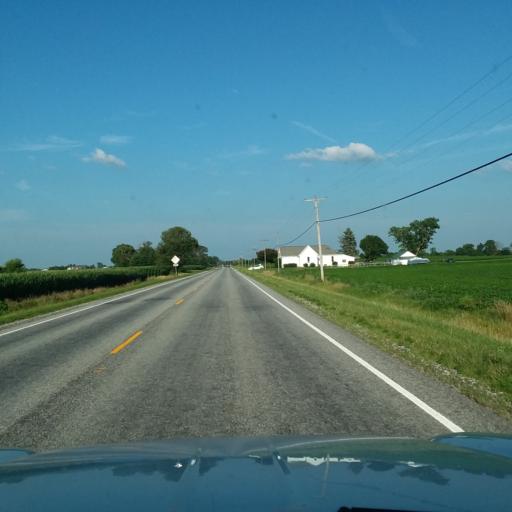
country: US
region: Indiana
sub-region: Johnson County
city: Princes Lakes
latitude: 39.4103
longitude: -86.0783
